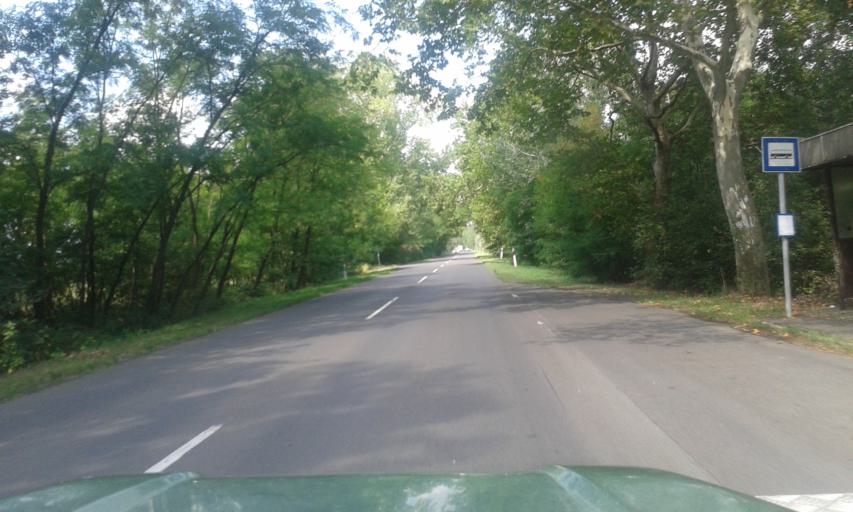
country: HU
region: Csongrad
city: Szatymaz
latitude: 46.3801
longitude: 20.0393
